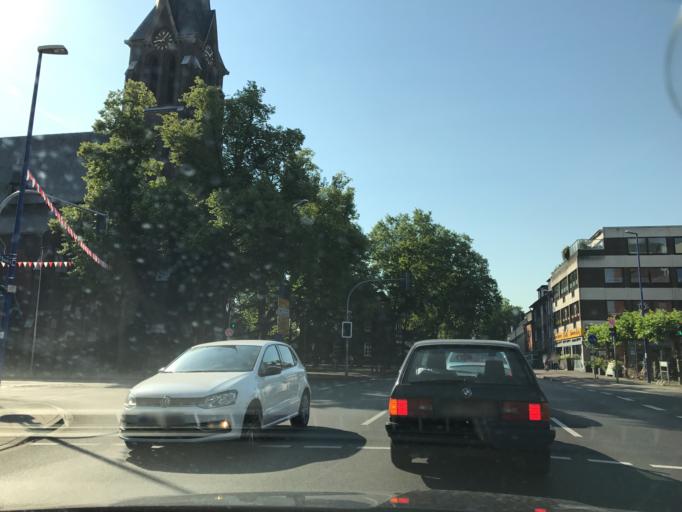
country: DE
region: North Rhine-Westphalia
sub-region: Regierungsbezirk Dusseldorf
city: Meerbusch
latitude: 51.2515
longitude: 6.6892
